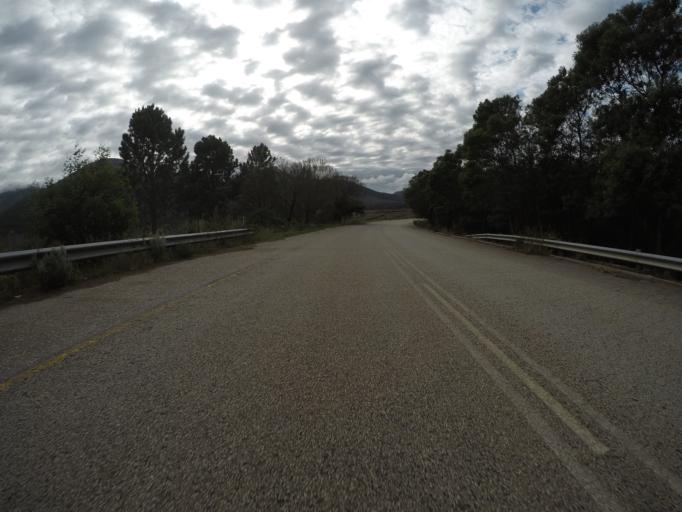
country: ZA
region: Eastern Cape
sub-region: Cacadu District Municipality
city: Kareedouw
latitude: -34.0121
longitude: 24.3093
